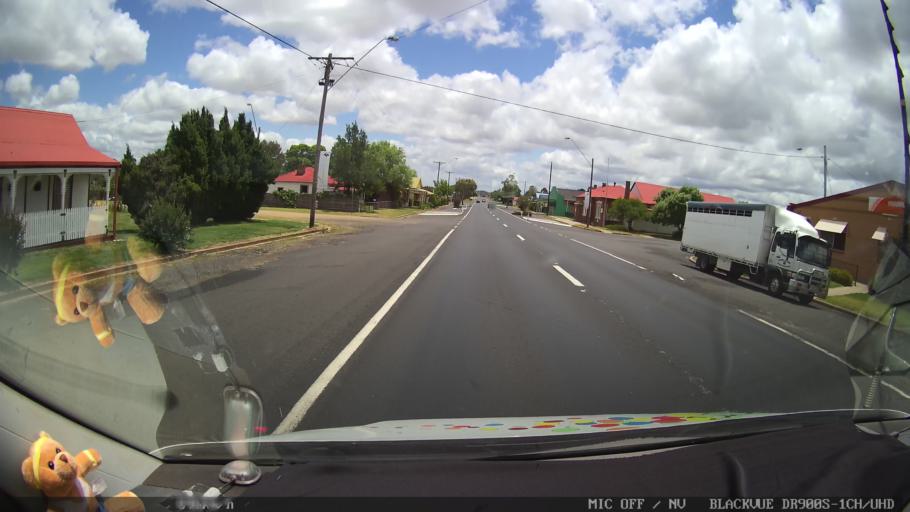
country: AU
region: New South Wales
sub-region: Glen Innes Severn
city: Glen Innes
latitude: -29.4411
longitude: 151.8464
